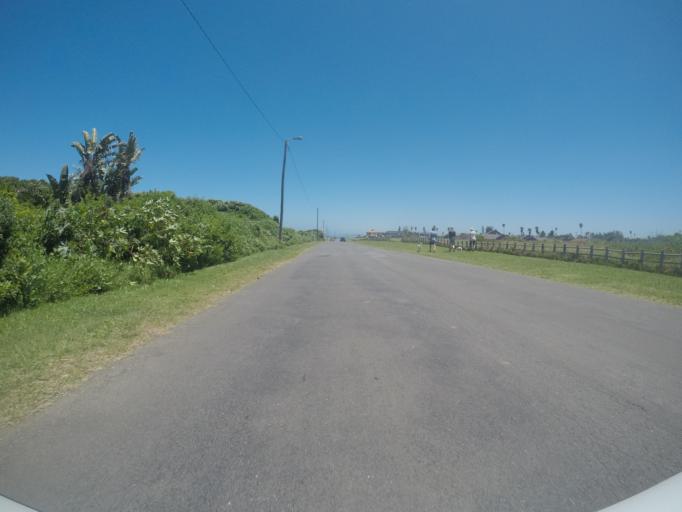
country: ZA
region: Eastern Cape
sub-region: Buffalo City Metropolitan Municipality
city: East London
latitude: -32.9520
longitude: 28.0136
